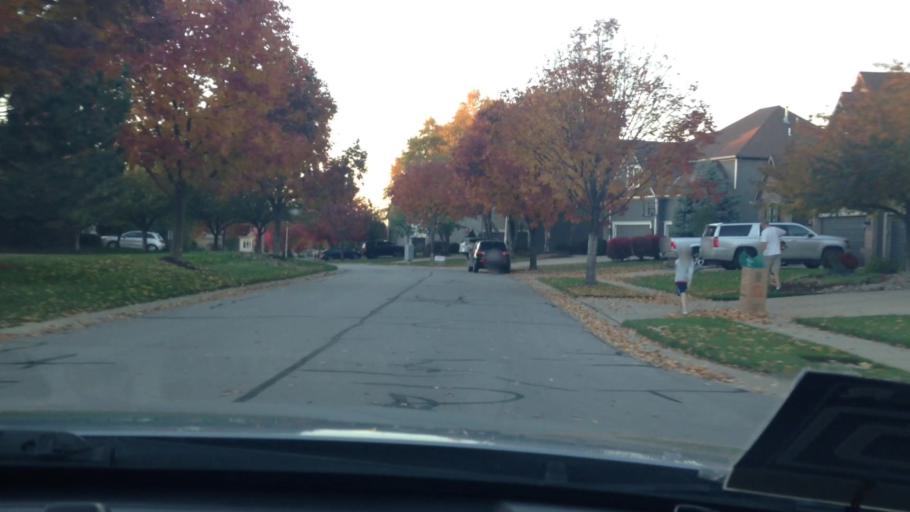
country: US
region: Kansas
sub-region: Johnson County
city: Lenexa
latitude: 38.8642
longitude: -94.7195
